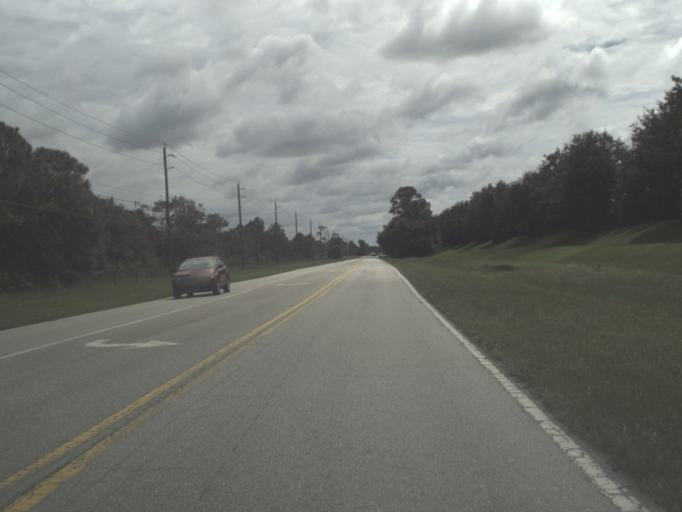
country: US
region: Florida
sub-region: Sarasota County
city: Plantation
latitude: 27.0899
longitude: -82.3377
